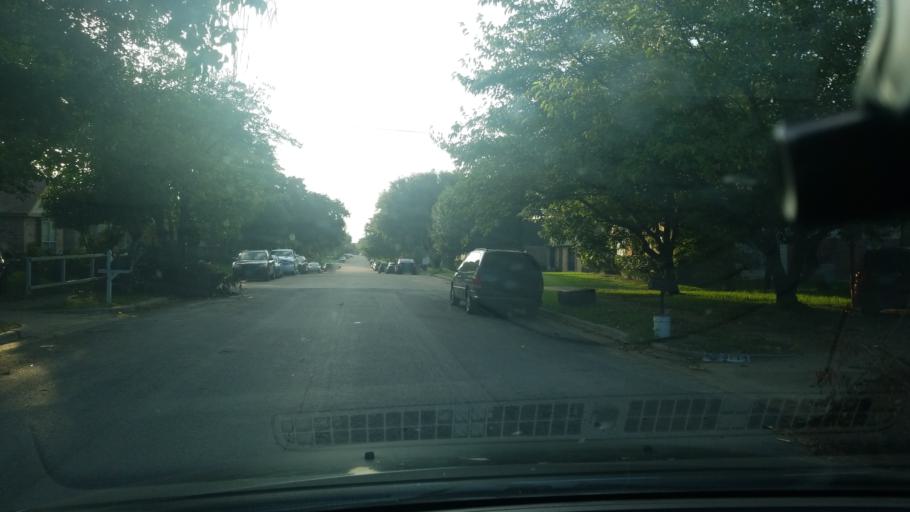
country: US
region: Texas
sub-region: Dallas County
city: Balch Springs
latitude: 32.7256
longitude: -96.6555
